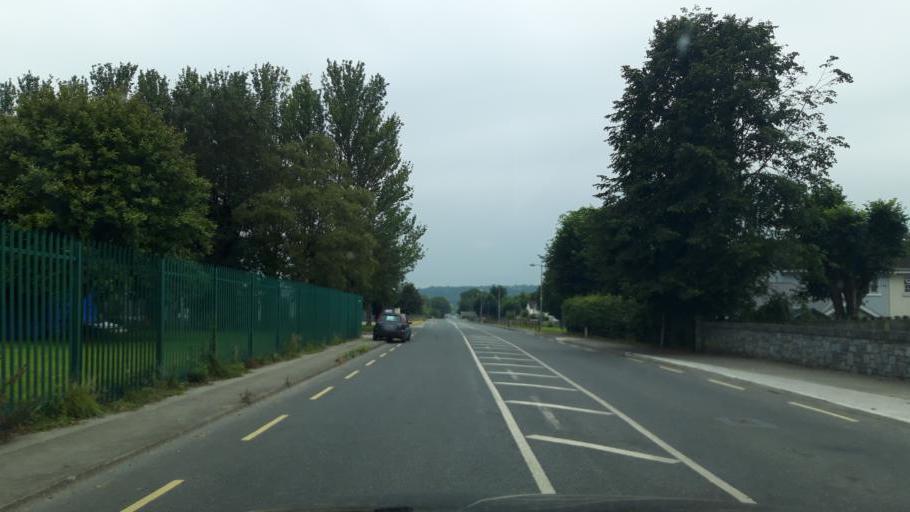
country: IE
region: Munster
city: Fethard
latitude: 52.4741
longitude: -7.6919
